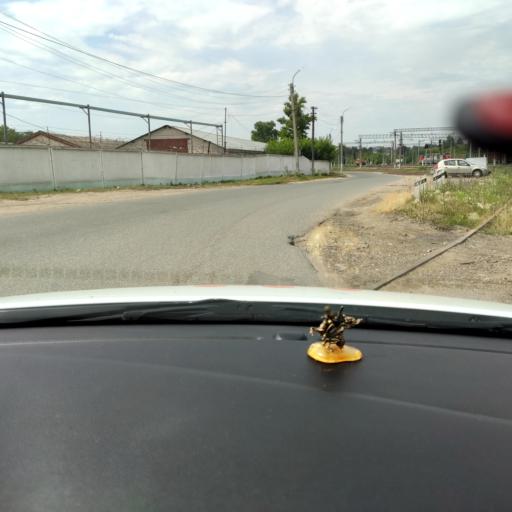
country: RU
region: Tatarstan
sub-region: Zelenodol'skiy Rayon
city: Zelenodolsk
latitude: 55.8412
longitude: 48.5593
